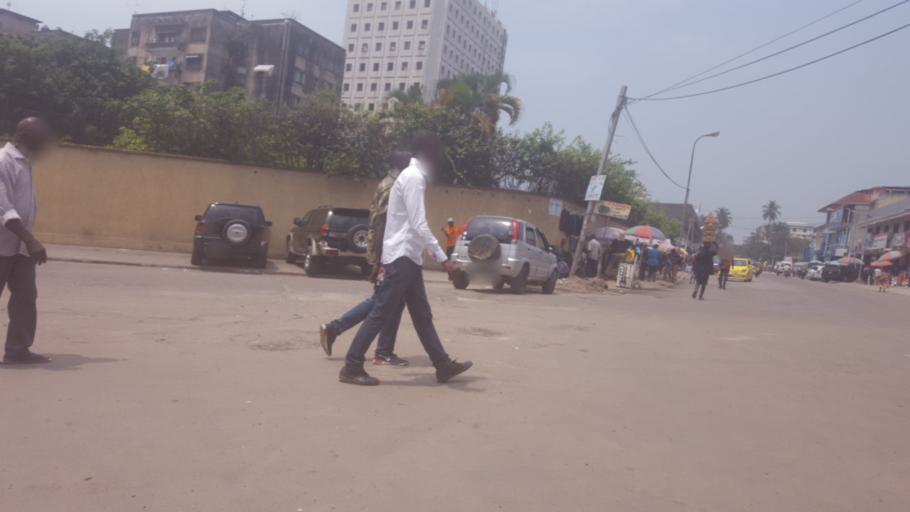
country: CD
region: Kinshasa
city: Kinshasa
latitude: -4.3048
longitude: 15.3124
